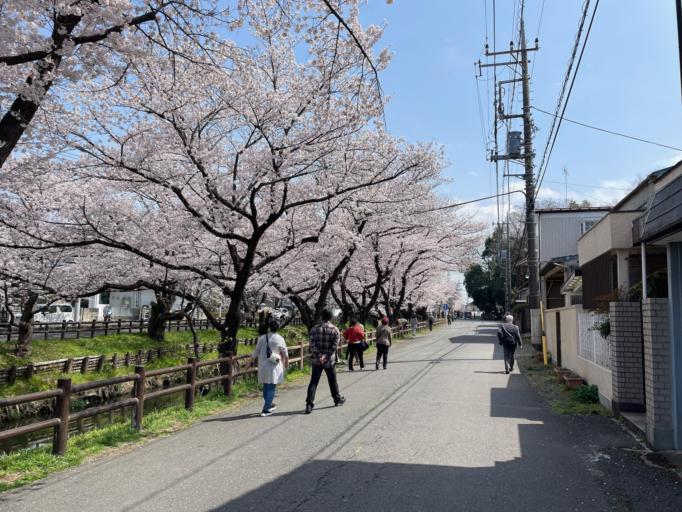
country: JP
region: Saitama
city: Kawagoe
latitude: 35.9285
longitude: 139.4876
